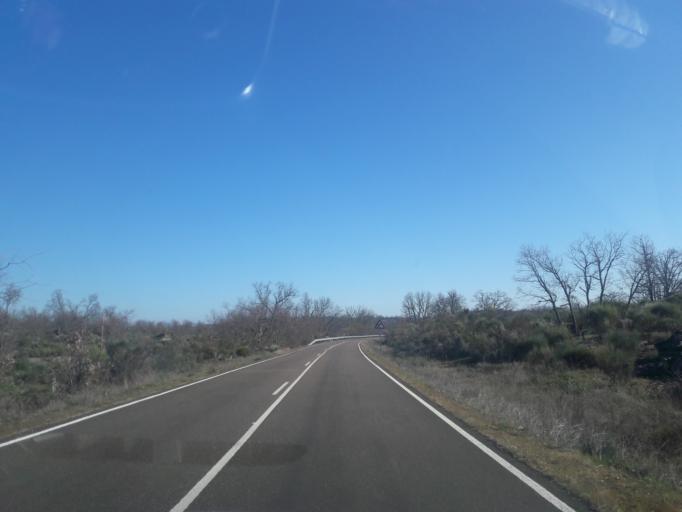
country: ES
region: Castille and Leon
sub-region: Provincia de Salamanca
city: Cabeza del Caballo
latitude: 41.0903
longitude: -6.5577
